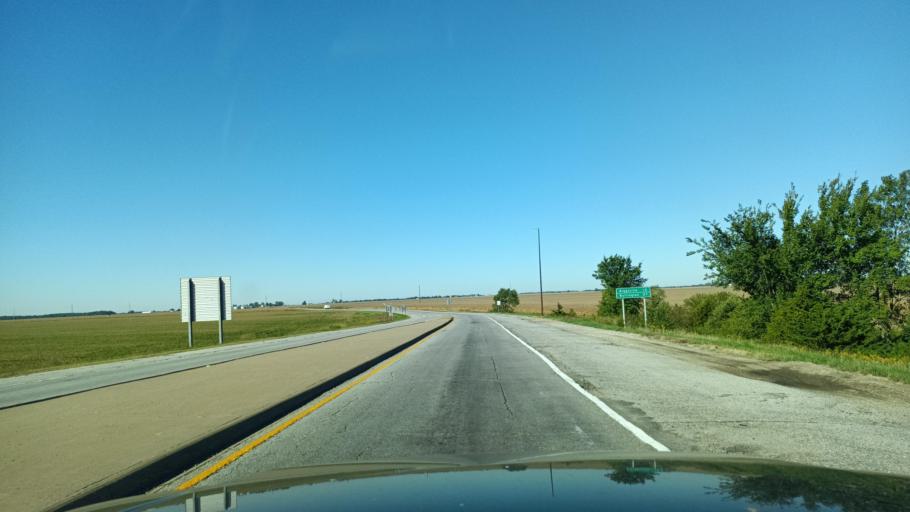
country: US
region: Illinois
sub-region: Warren County
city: Monmouth
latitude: 40.8907
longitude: -90.6645
